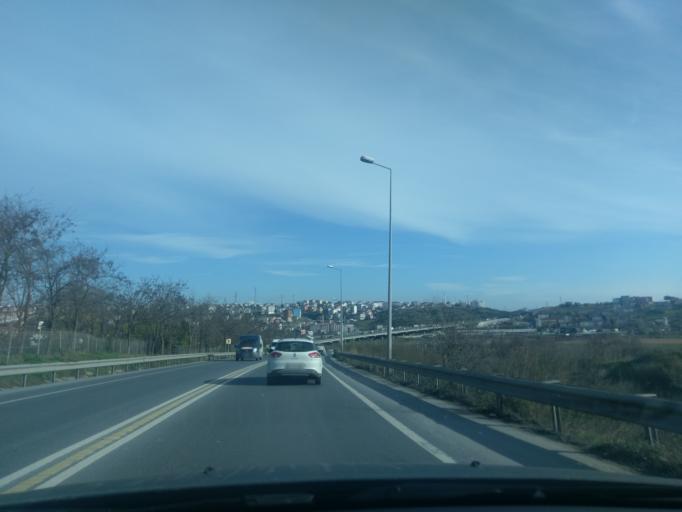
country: TR
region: Istanbul
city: Esenyurt
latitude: 41.0598
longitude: 28.7362
